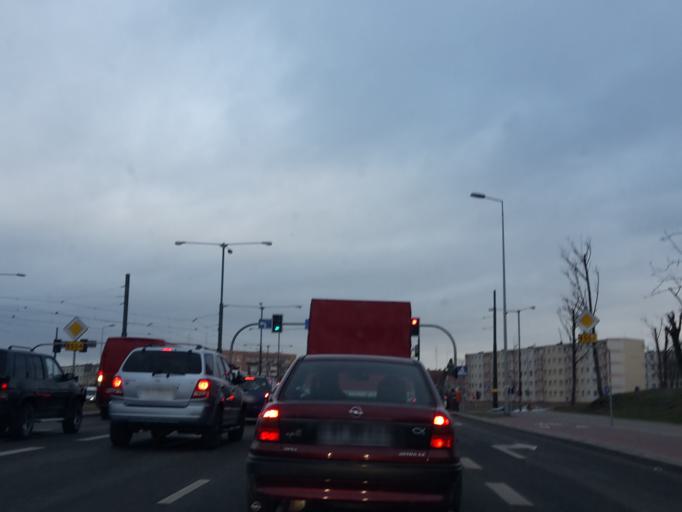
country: PL
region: Warmian-Masurian Voivodeship
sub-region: Powiat elblaski
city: Elblag
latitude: 54.1654
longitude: 19.4060
